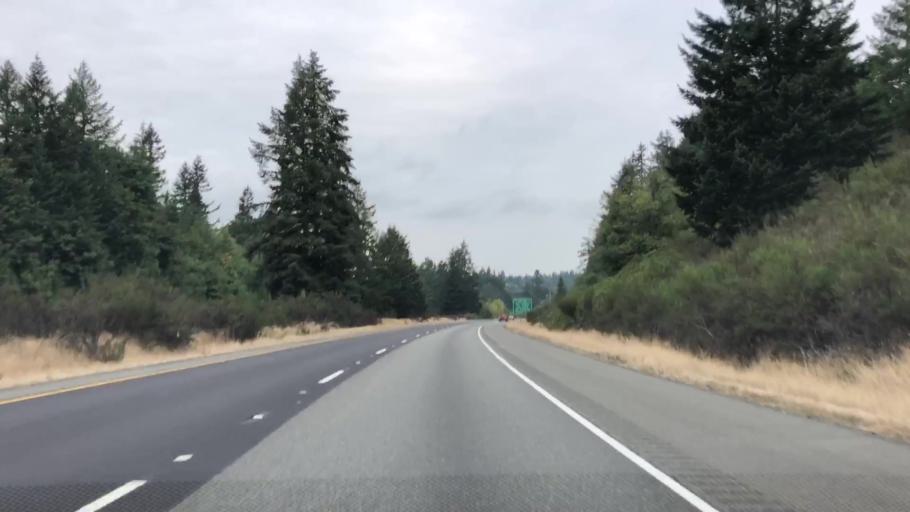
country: US
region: Washington
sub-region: Kitsap County
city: Port Orchard
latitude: 47.5162
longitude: -122.6569
